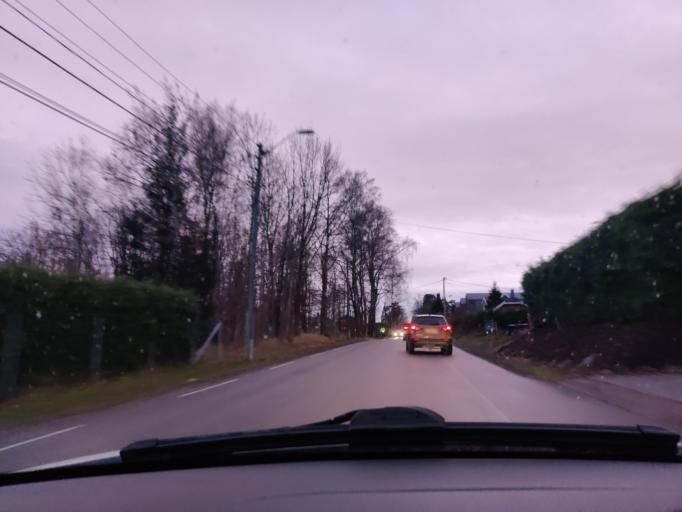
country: NO
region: Vestfold
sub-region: Tonsberg
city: Sem
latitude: 59.2688
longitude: 10.3655
